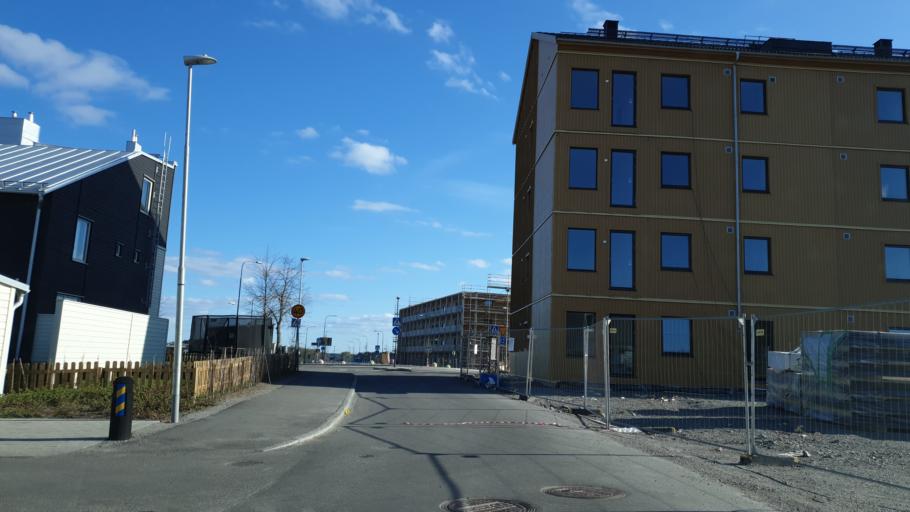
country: SE
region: Stockholm
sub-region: Upplands Vasby Kommun
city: Upplands Vaesby
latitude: 59.5140
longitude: 17.8736
